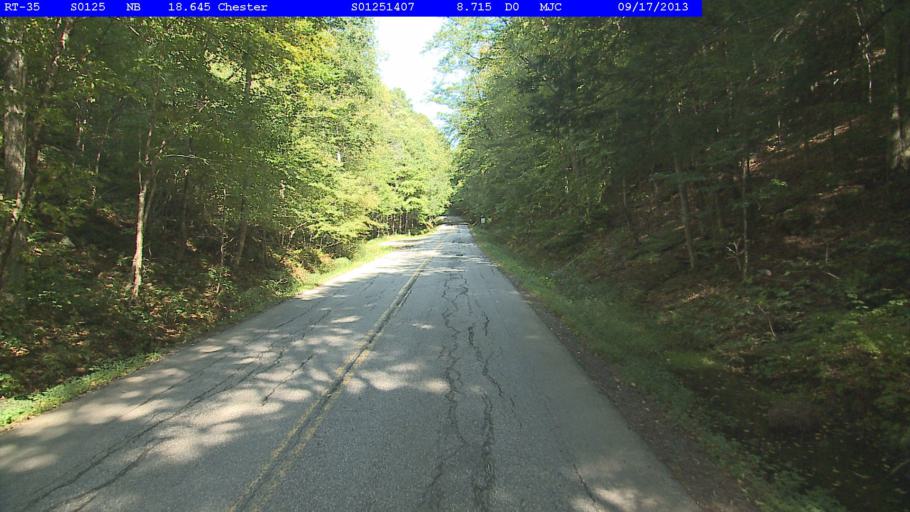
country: US
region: Vermont
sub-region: Windsor County
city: Chester
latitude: 43.2312
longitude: -72.6066
